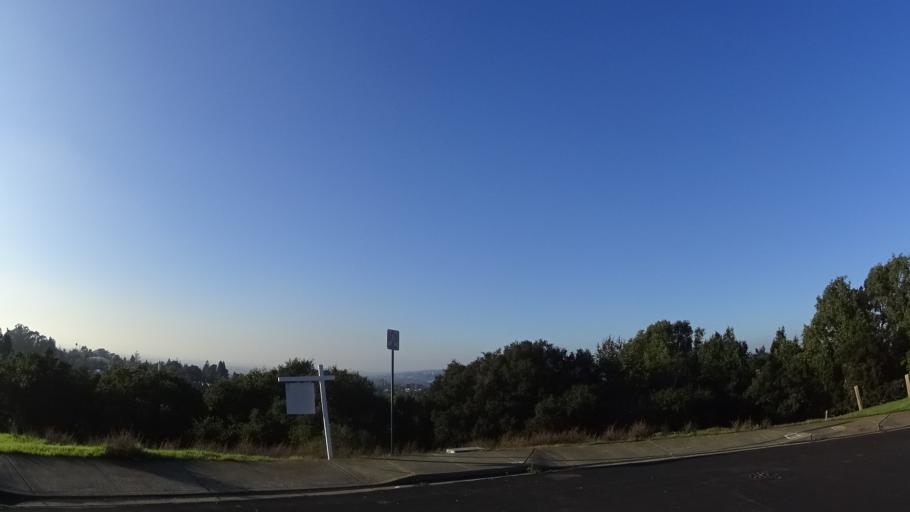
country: US
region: California
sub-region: Alameda County
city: Fairview
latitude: 37.6606
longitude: -122.0506
